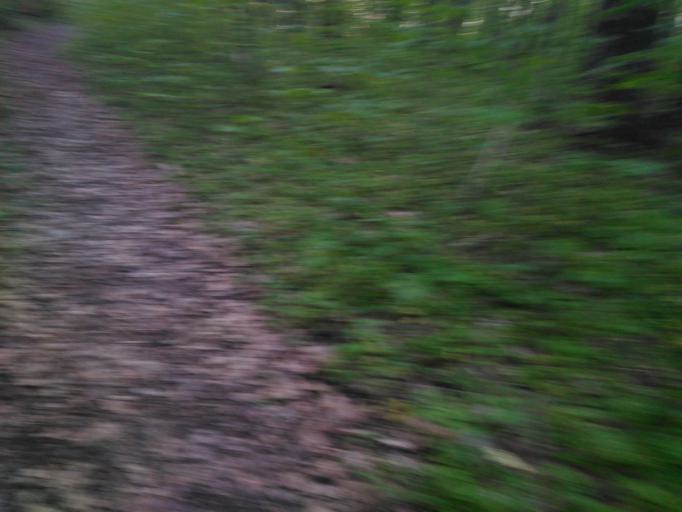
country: RU
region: Ulyanovsk
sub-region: Ulyanovskiy Rayon
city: Ulyanovsk
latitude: 54.2725
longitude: 48.3378
